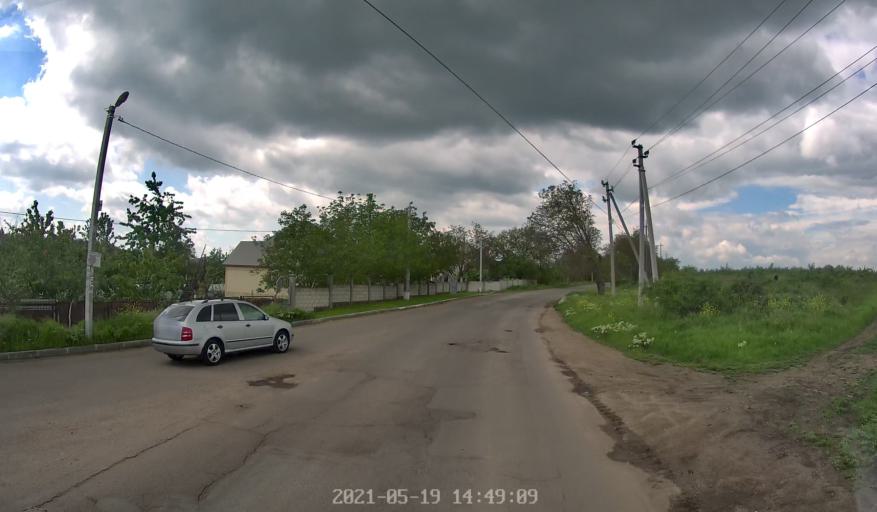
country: MD
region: Chisinau
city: Stauceni
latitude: 47.0478
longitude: 28.9539
